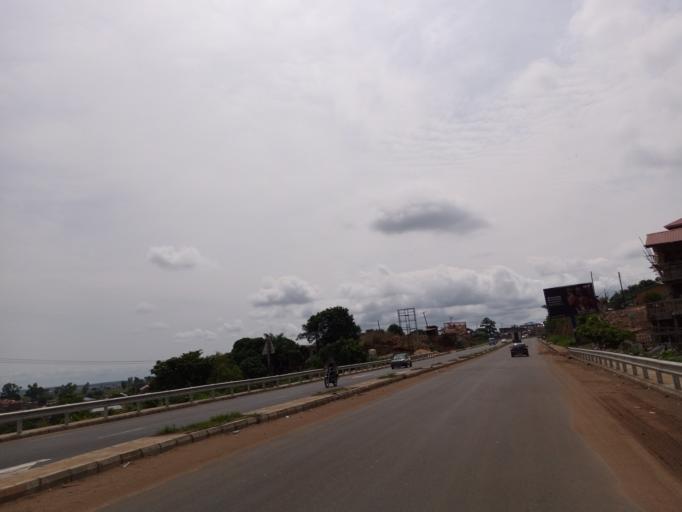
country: SL
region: Western Area
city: Hastings
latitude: 8.3880
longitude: -13.1285
